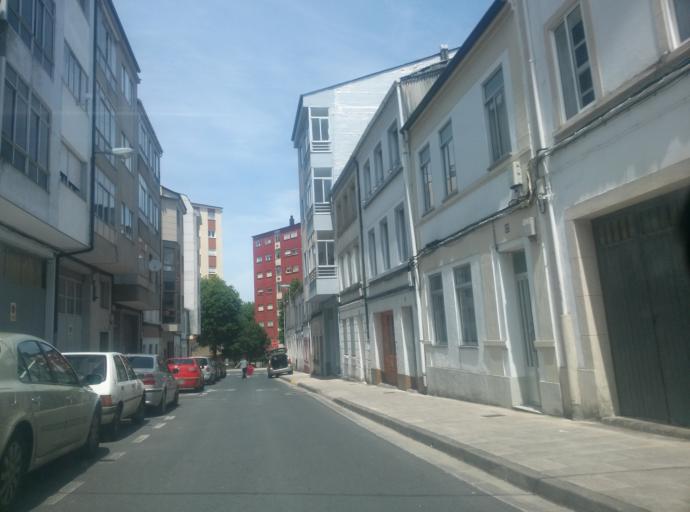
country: ES
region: Galicia
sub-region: Provincia de Lugo
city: Lugo
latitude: 43.0218
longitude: -7.5609
